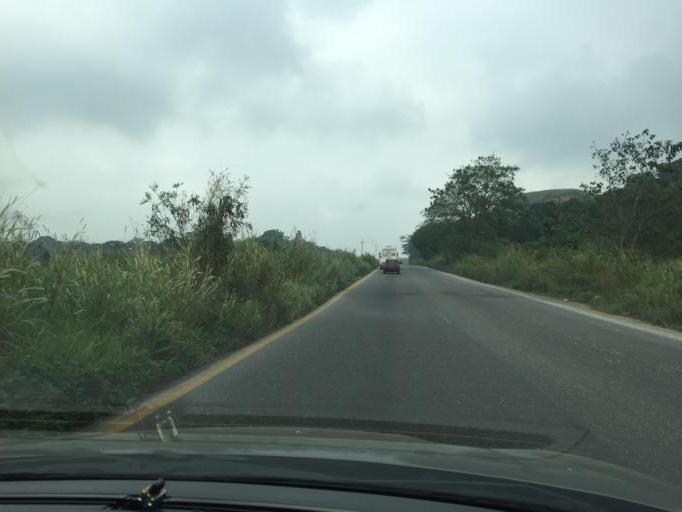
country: MX
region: Veracruz
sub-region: Moloacan
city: Tlacuilolapan
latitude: 18.0750
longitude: -94.2767
